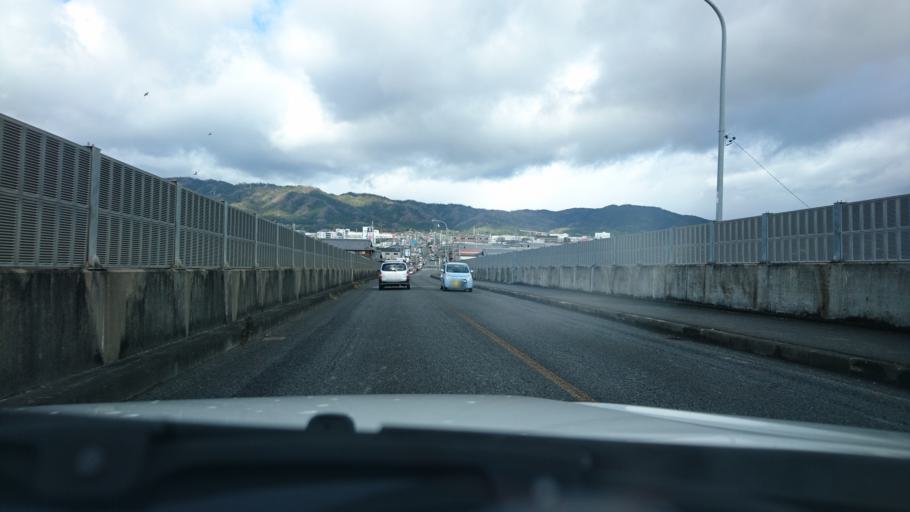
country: JP
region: Mie
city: Ueno-ebisumachi
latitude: 34.7707
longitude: 136.1236
